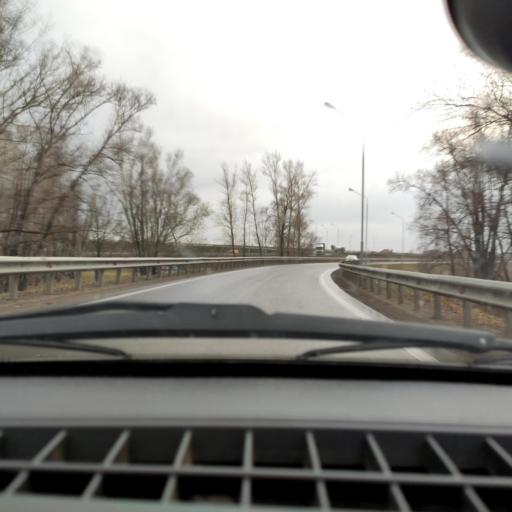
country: RU
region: Bashkortostan
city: Ufa
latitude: 54.6471
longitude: 55.9318
